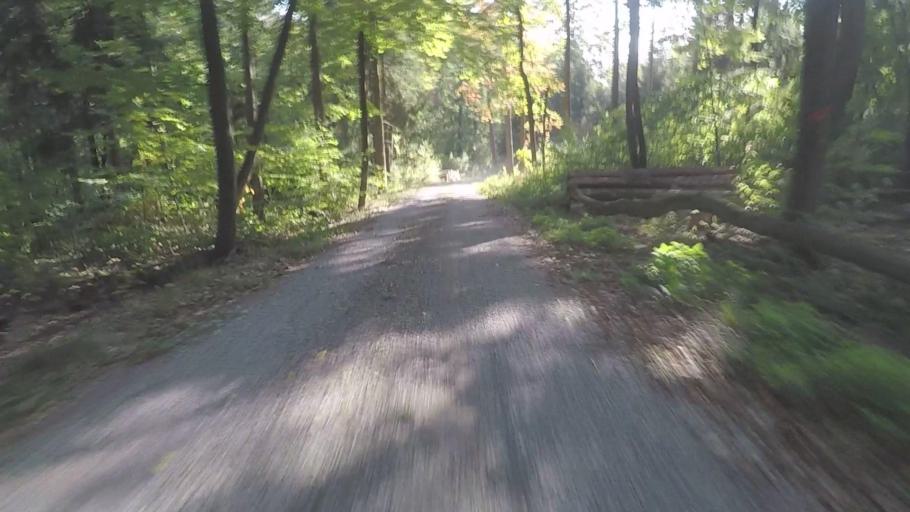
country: DE
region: Baden-Wuerttemberg
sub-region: Regierungsbezirk Stuttgart
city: Grosserlach
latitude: 49.0393
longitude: 9.4840
